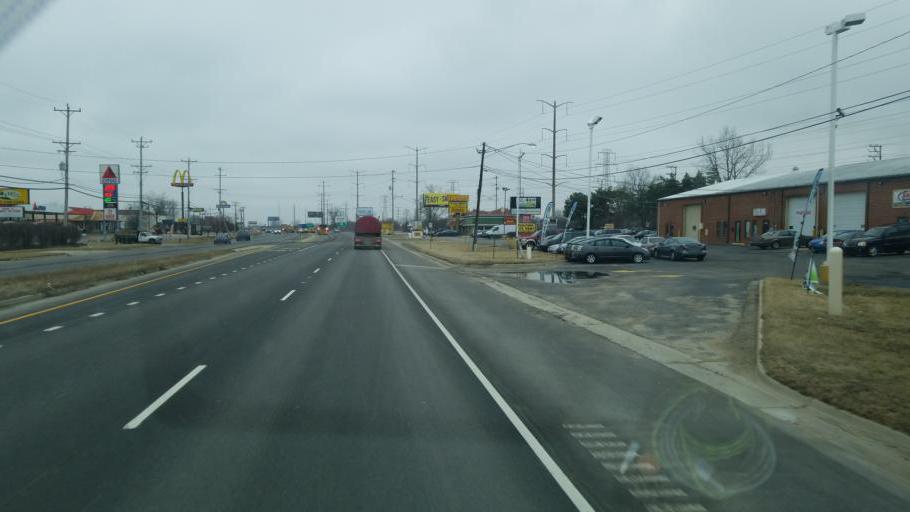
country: US
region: Illinois
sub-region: Lake County
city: Knollwood
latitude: 42.3024
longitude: -87.8755
